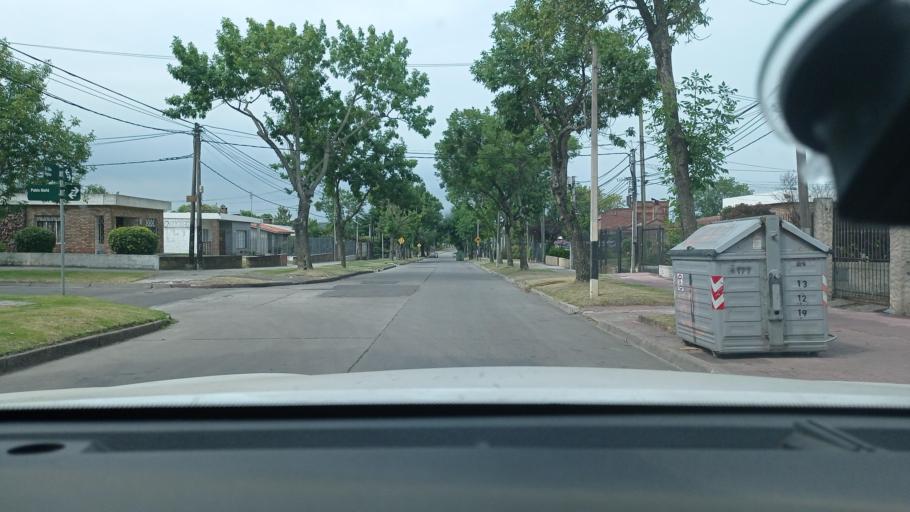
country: UY
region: Canelones
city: Paso de Carrasco
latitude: -34.8748
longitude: -56.0913
